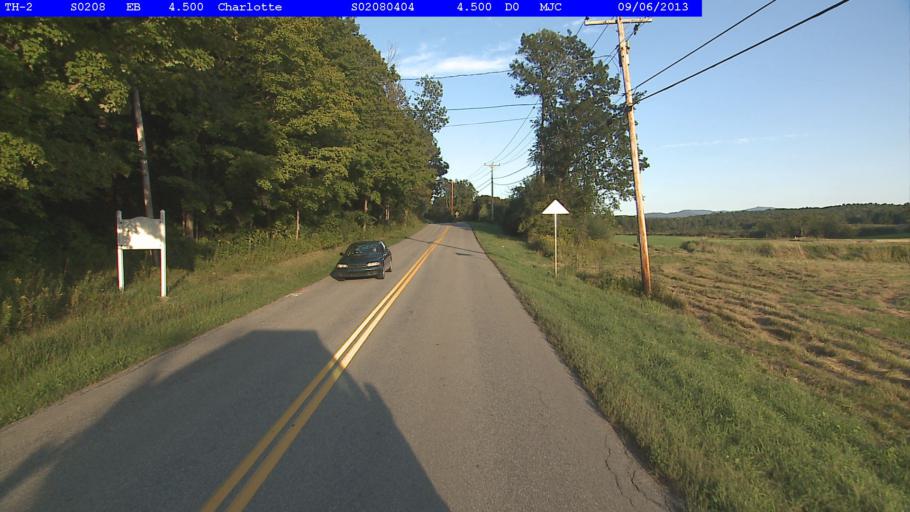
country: US
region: Vermont
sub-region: Chittenden County
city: Hinesburg
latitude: 44.3229
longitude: -73.1585
